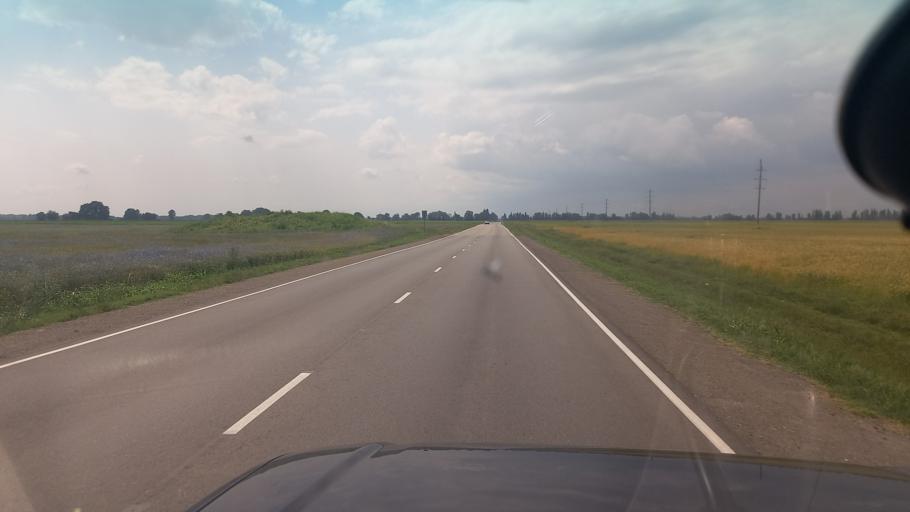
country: RU
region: Adygeya
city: Koshekhabl'
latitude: 44.9055
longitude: 40.4652
